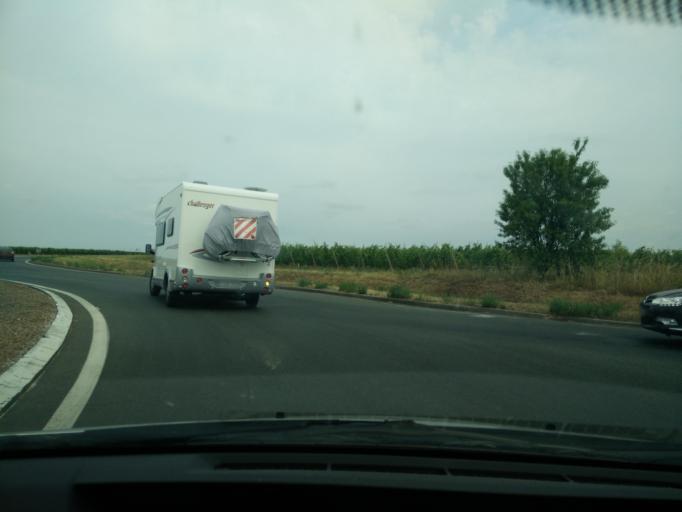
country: FR
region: Pays de la Loire
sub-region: Departement de Maine-et-Loire
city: Montreuil-Bellay
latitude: 47.1399
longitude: -0.1587
